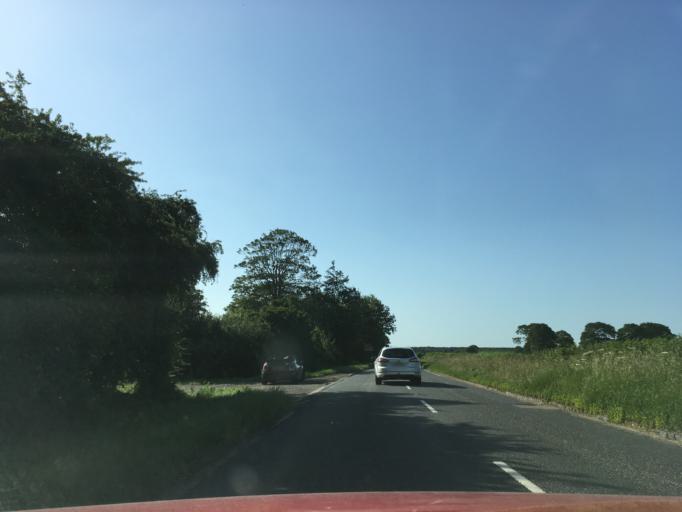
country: GB
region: England
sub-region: Oxfordshire
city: Somerton
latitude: 51.9134
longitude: -1.2353
